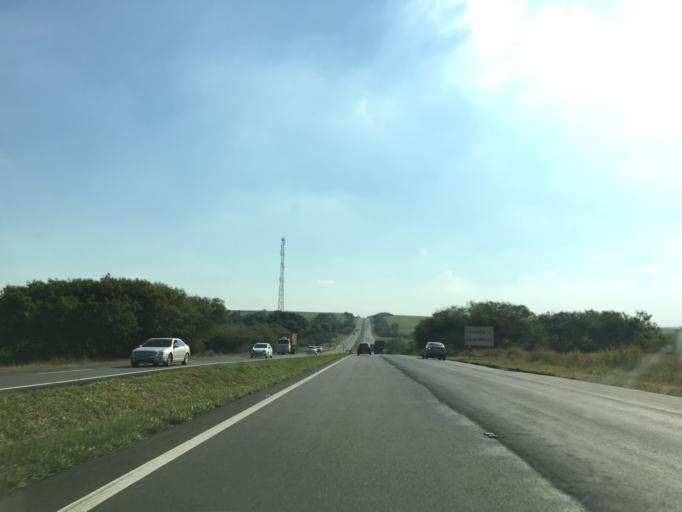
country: BR
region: Sao Paulo
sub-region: Piracicaba
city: Piracicaba
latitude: -22.7270
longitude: -47.5541
